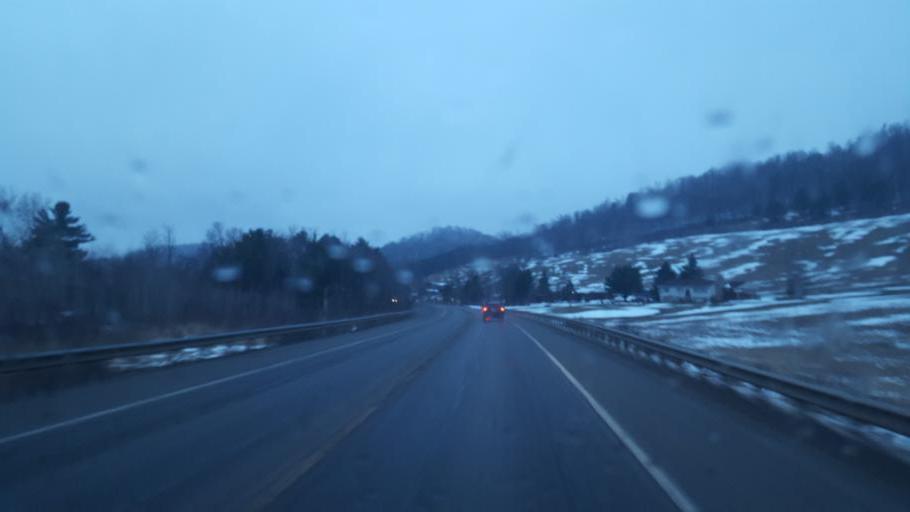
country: US
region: Pennsylvania
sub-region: McKean County
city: Port Allegany
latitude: 41.7888
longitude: -78.1722
